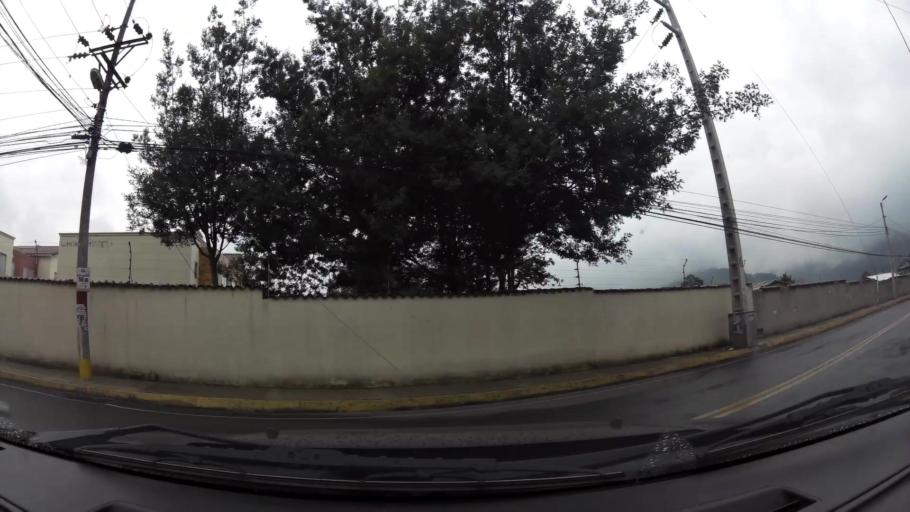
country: EC
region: Pichincha
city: Sangolqui
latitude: -0.2686
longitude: -78.4618
